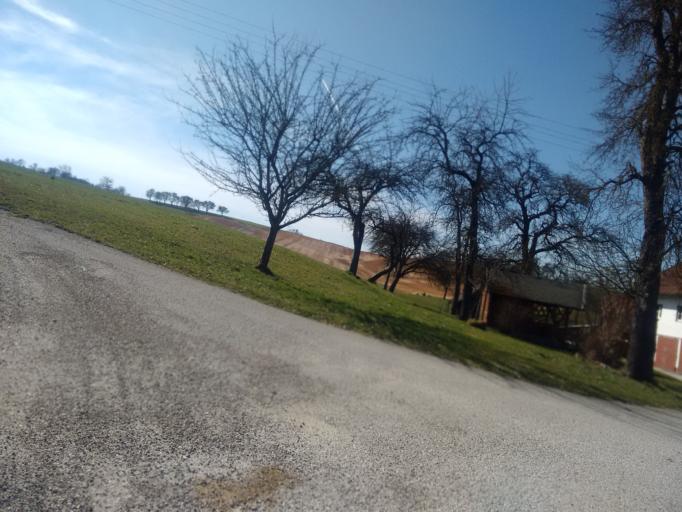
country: AT
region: Upper Austria
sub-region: Politischer Bezirk Grieskirchen
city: Bad Schallerbach
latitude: 48.2056
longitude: 13.9540
